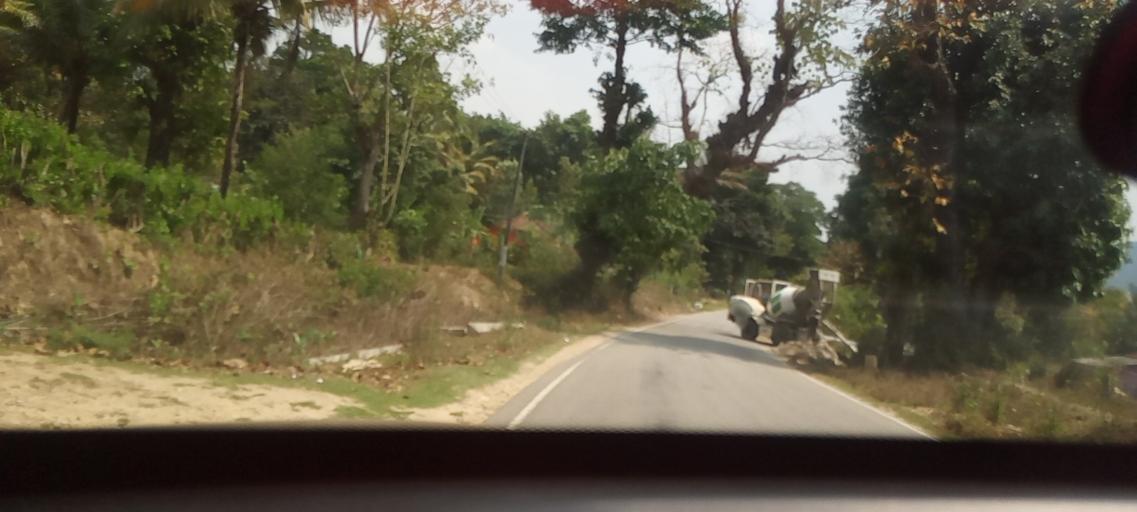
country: IN
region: Karnataka
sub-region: Chikmagalur
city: Mudigere
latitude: 13.2962
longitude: 75.5929
